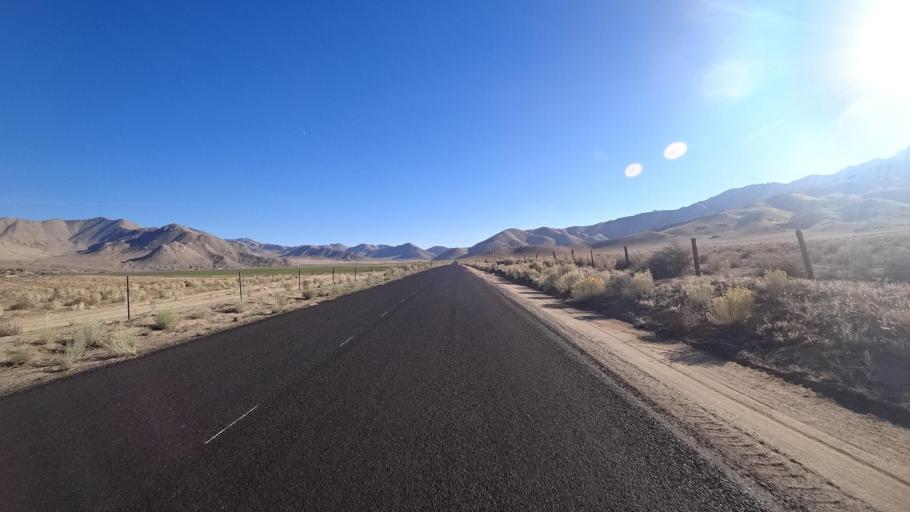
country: US
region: California
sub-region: Kern County
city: Weldon
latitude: 35.6423
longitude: -118.2691
